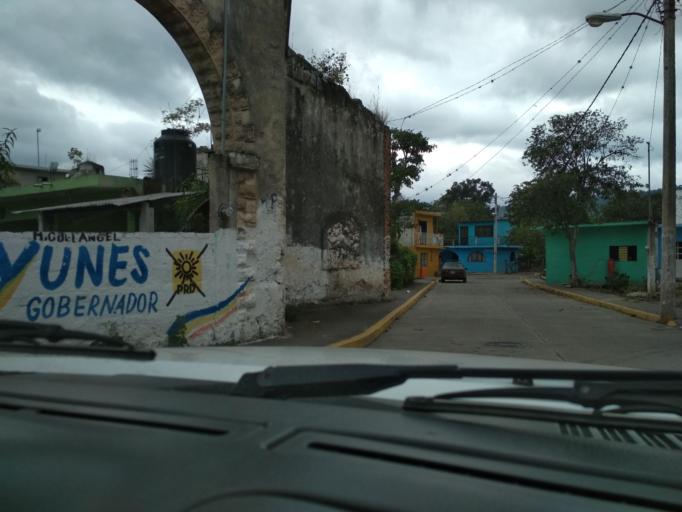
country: MX
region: Veracruz
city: El Castillo
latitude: 19.5818
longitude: -96.8383
